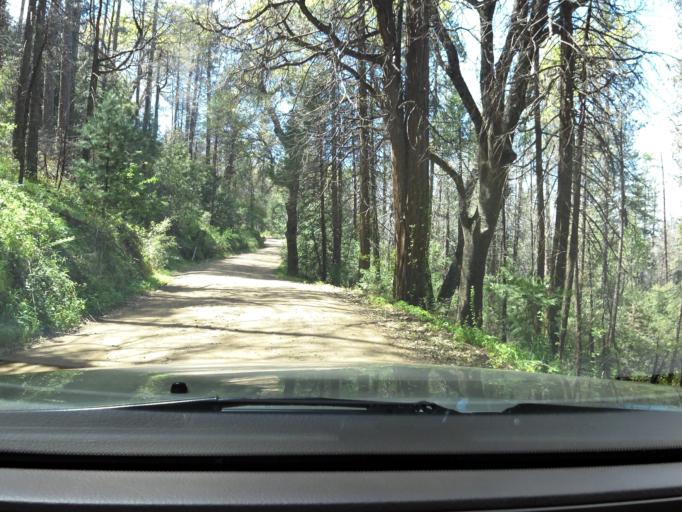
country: US
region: California
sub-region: Madera County
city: Oakhurst
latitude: 37.2817
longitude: -119.5950
